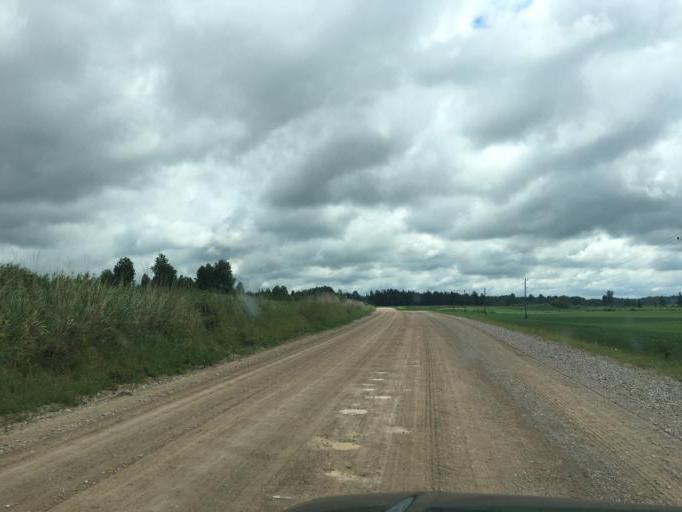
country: LV
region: Balvu Rajons
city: Balvi
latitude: 57.3406
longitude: 27.3485
